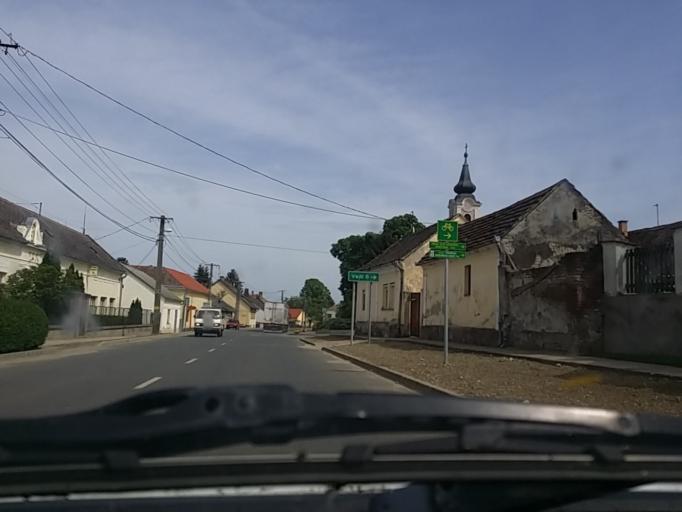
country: HU
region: Baranya
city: Vajszlo
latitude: 45.8602
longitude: 17.9817
